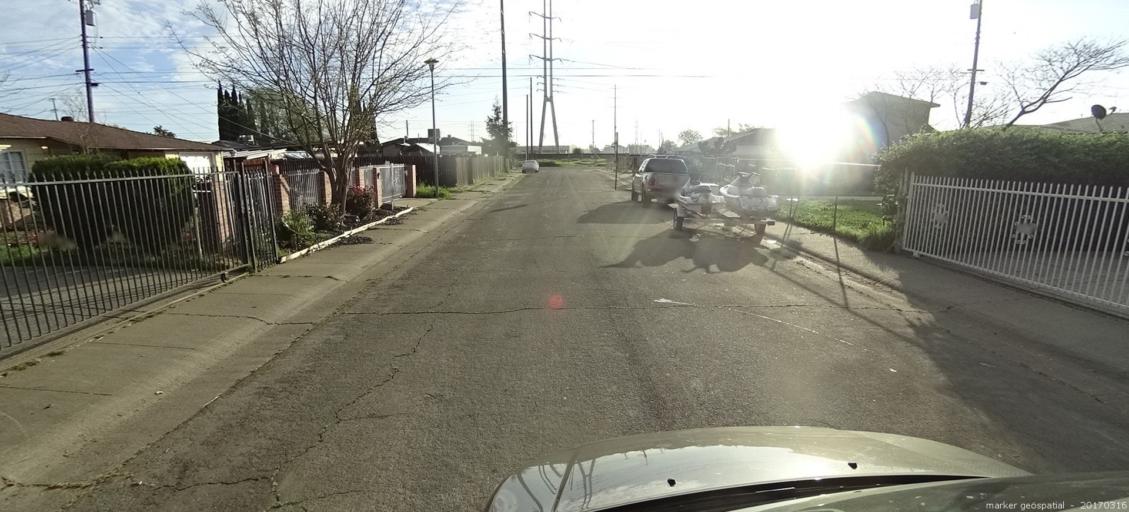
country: US
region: California
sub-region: Sacramento County
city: Parkway
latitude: 38.5046
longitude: -121.4751
